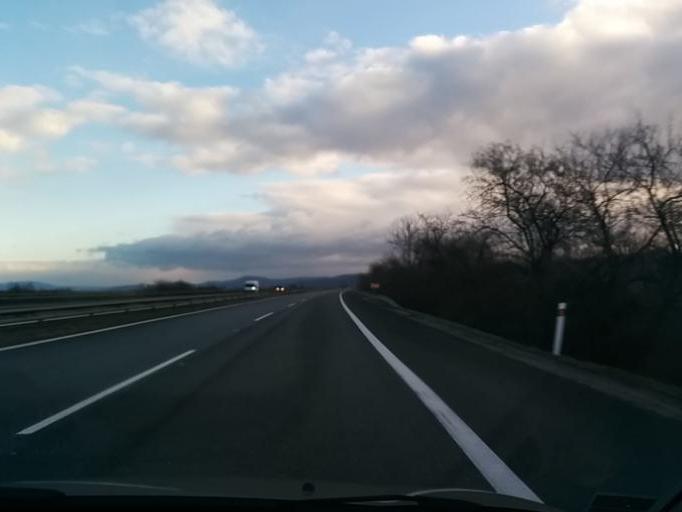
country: SK
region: Trnavsky
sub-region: Okres Trnava
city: Piestany
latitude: 48.6416
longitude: 17.8173
